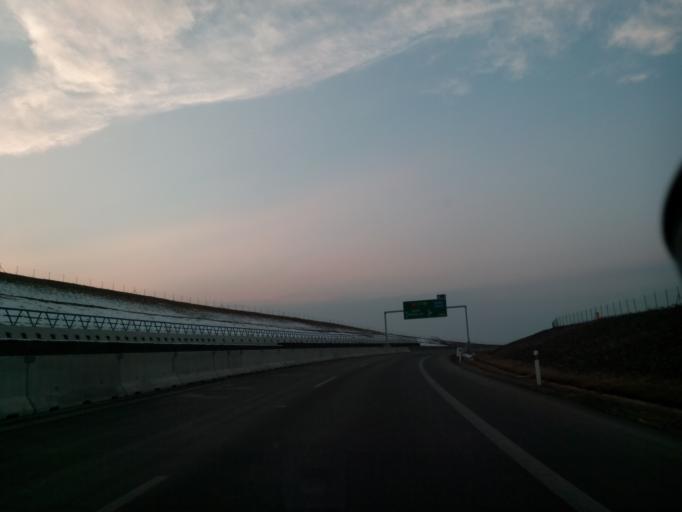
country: HU
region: Borsod-Abauj-Zemplen
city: Gonc
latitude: 48.5420
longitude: 21.2371
